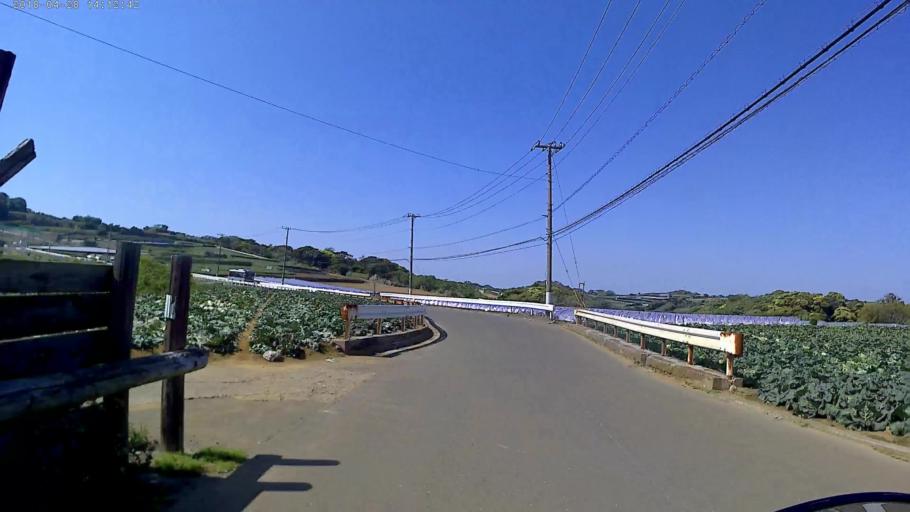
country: JP
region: Kanagawa
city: Miura
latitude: 35.1481
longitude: 139.6514
